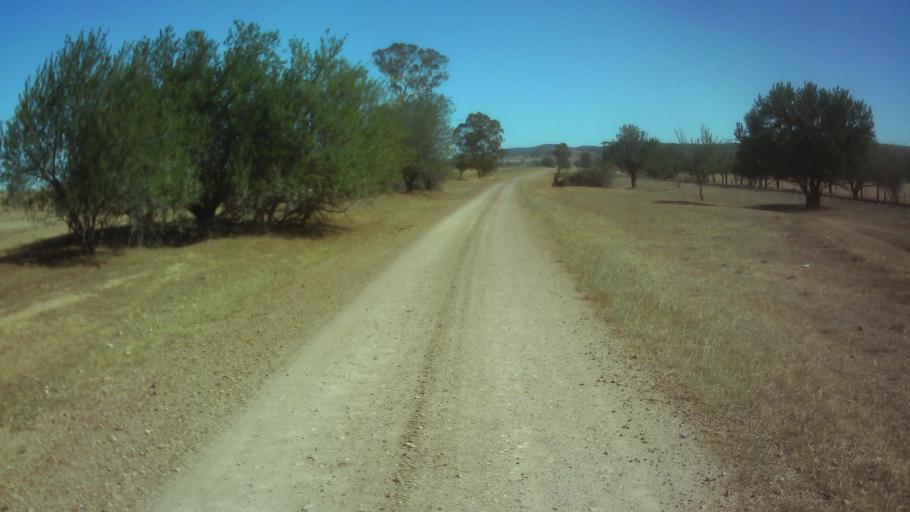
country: AU
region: New South Wales
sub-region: Weddin
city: Grenfell
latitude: -33.9609
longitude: 148.3041
